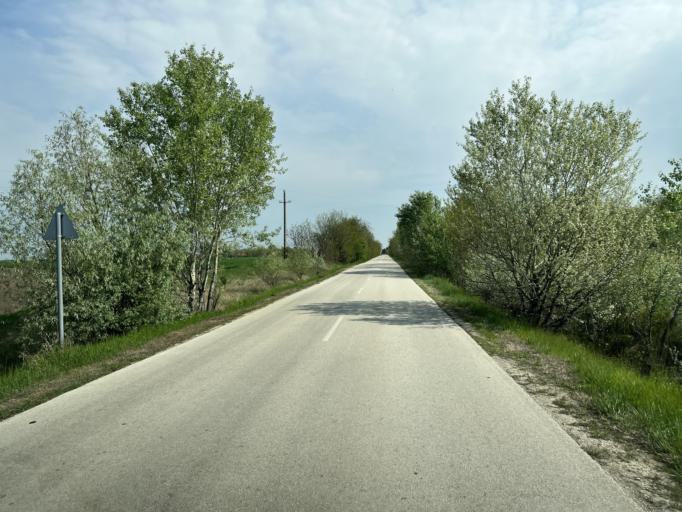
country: HU
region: Pest
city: Jaszkarajeno
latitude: 47.0865
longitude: 20.0164
